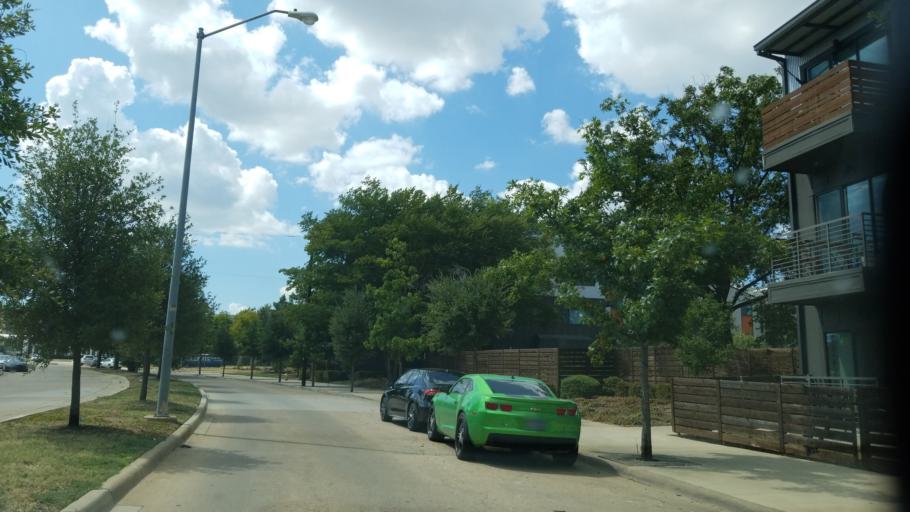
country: US
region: Texas
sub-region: Dallas County
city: Dallas
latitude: 32.7715
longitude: -96.8302
